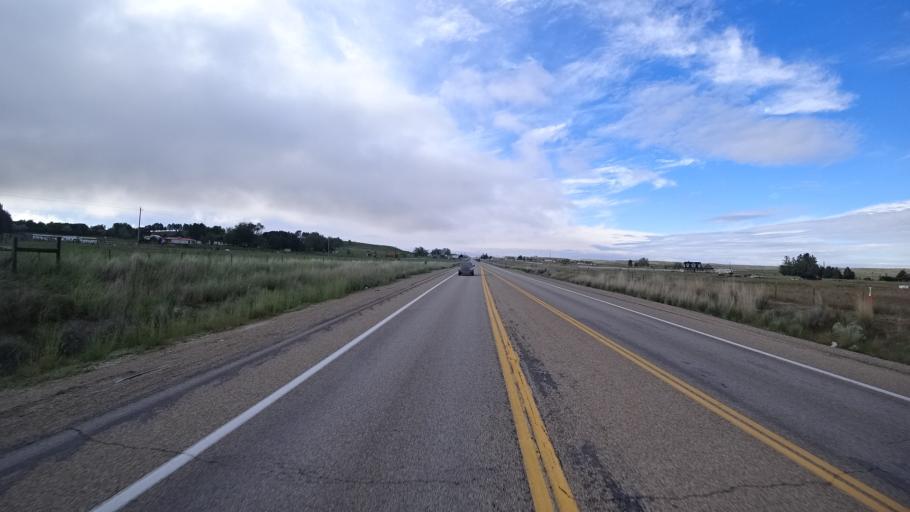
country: US
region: Idaho
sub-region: Ada County
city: Star
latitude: 43.7778
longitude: -116.4713
